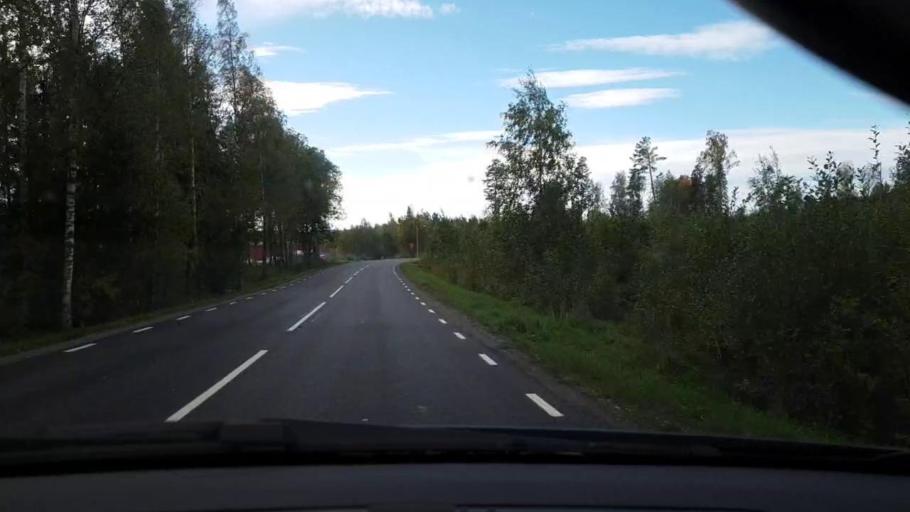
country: SE
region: Dalarna
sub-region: Borlange Kommun
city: Ornas
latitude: 60.5089
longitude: 15.5220
